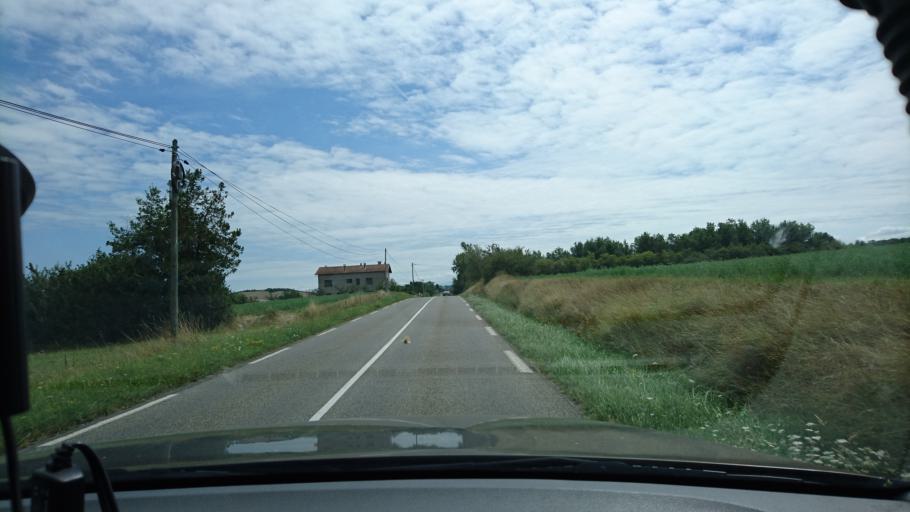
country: FR
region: Midi-Pyrenees
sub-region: Departement de l'Ariege
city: Lezat-sur-Leze
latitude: 43.3007
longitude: 1.3351
